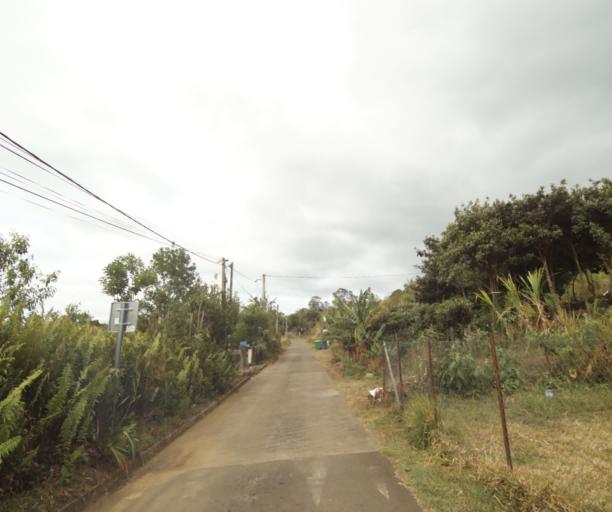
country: RE
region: Reunion
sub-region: Reunion
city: Saint-Paul
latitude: -21.0176
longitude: 55.3283
